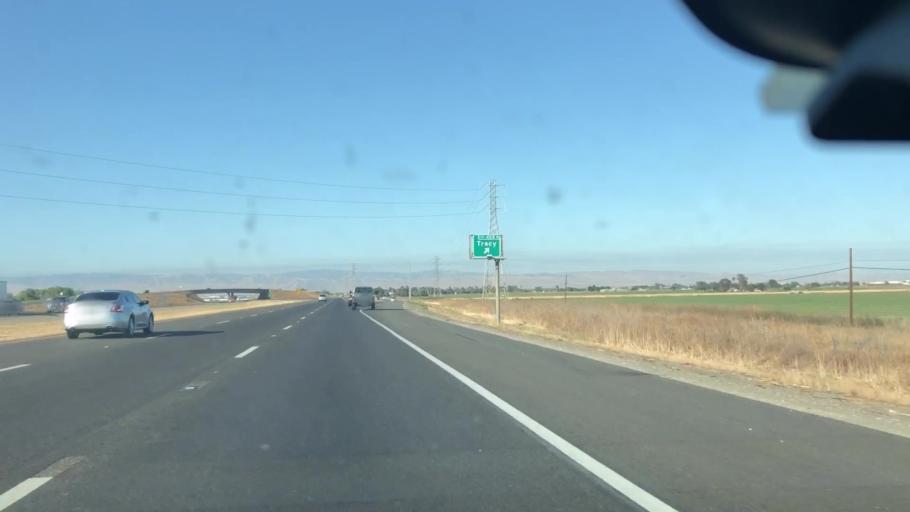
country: US
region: California
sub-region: San Joaquin County
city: Lathrop
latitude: 37.7632
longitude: -121.3382
